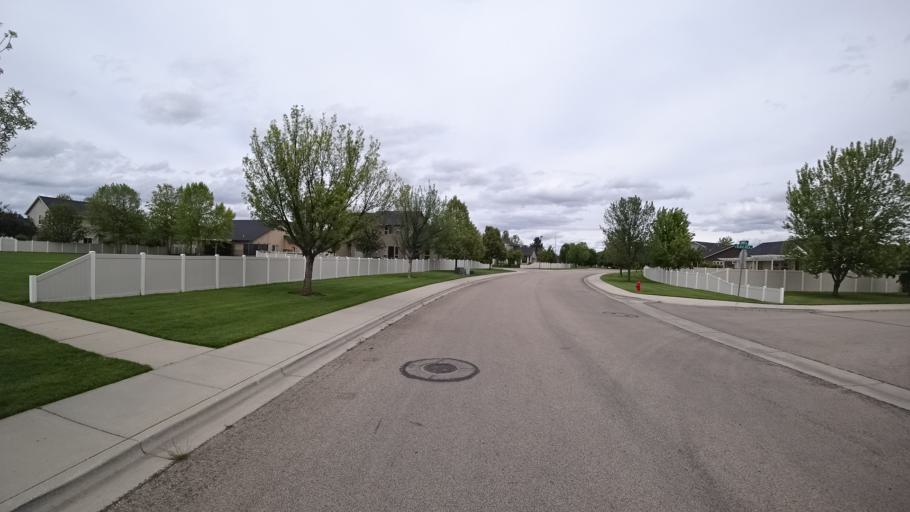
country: US
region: Idaho
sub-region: Ada County
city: Meridian
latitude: 43.6453
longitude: -116.4020
